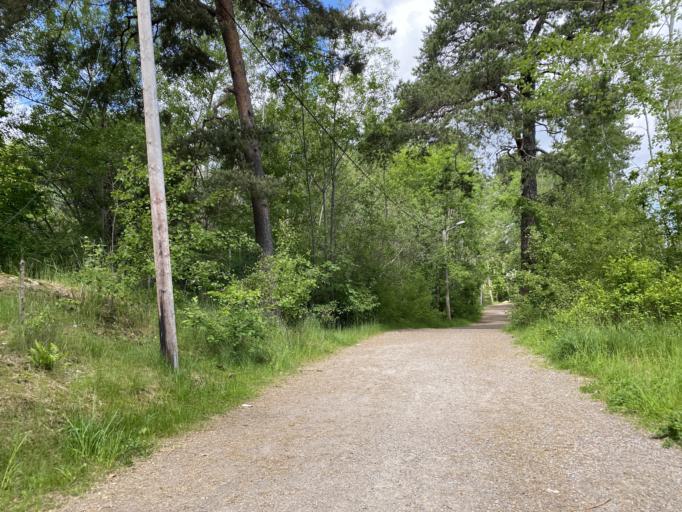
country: SE
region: Stockholm
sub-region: Jarfalla Kommun
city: Jakobsberg
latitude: 59.3749
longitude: 17.8517
